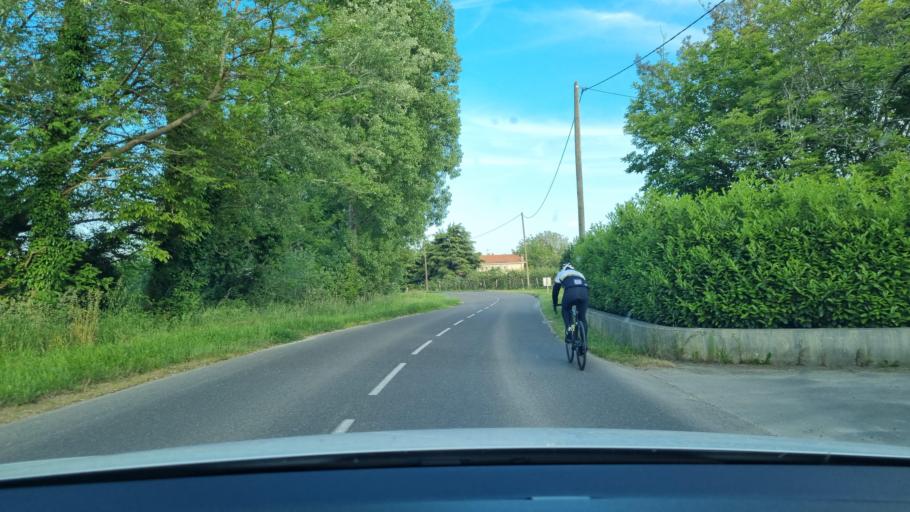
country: FR
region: Aquitaine
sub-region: Departement des Landes
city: Peyrehorade
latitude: 43.5411
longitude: -1.1287
